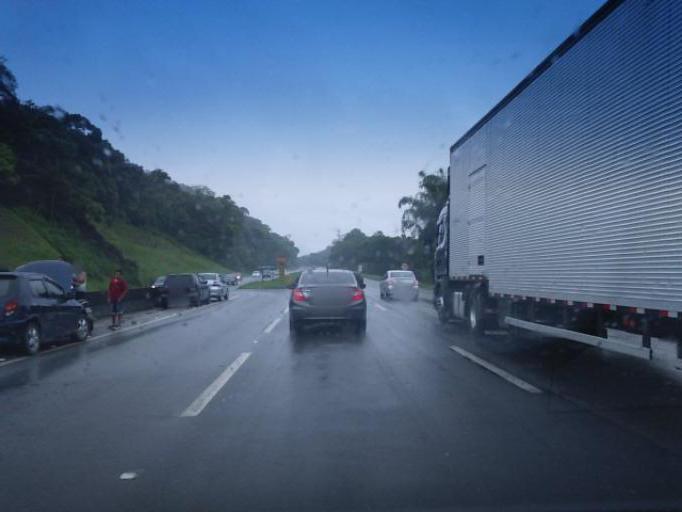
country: BR
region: Santa Catarina
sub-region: Joinville
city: Joinville
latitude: -26.0927
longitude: -48.8648
